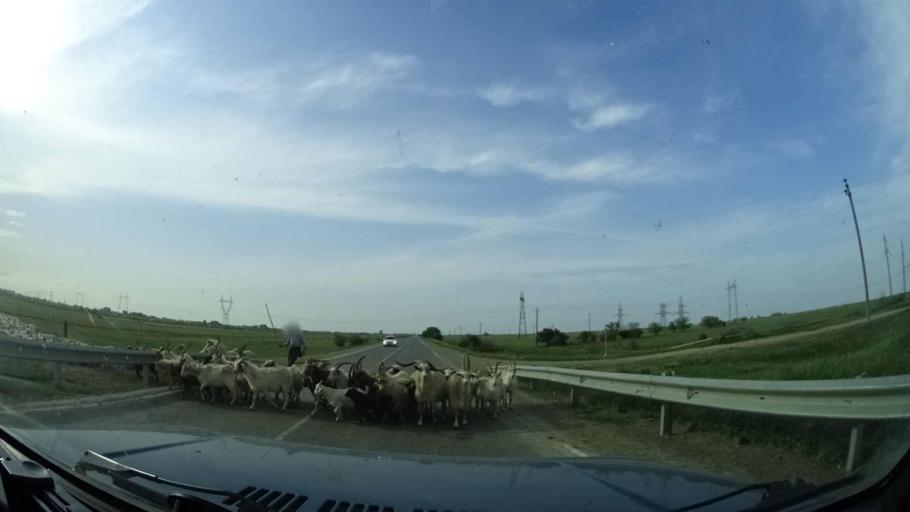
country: RU
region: Dagestan
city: Babayurt
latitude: 43.5072
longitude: 46.7405
